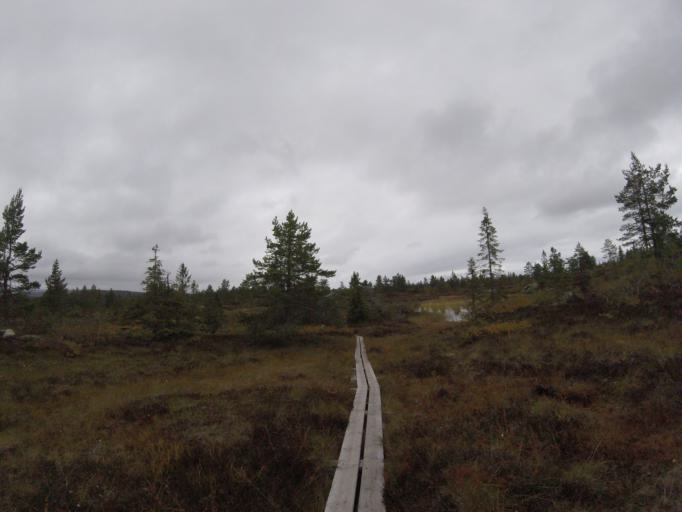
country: NO
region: Buskerud
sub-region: Flesberg
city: Lampeland
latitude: 59.7583
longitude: 9.4010
